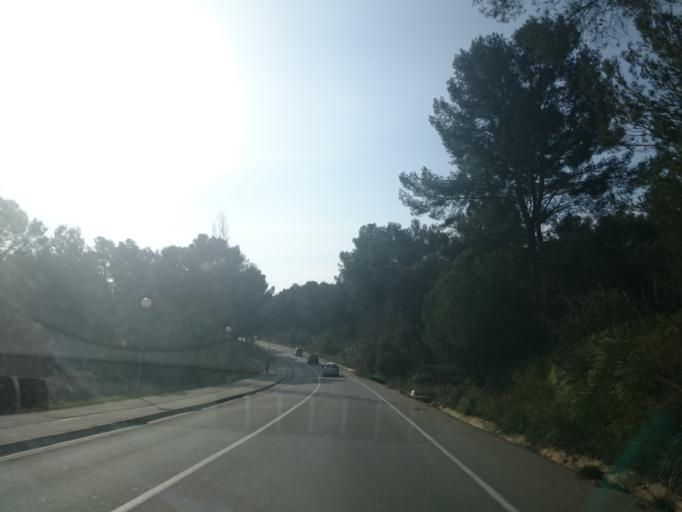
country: ES
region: Catalonia
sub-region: Provincia de Barcelona
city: Gava
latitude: 41.3032
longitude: 1.9895
